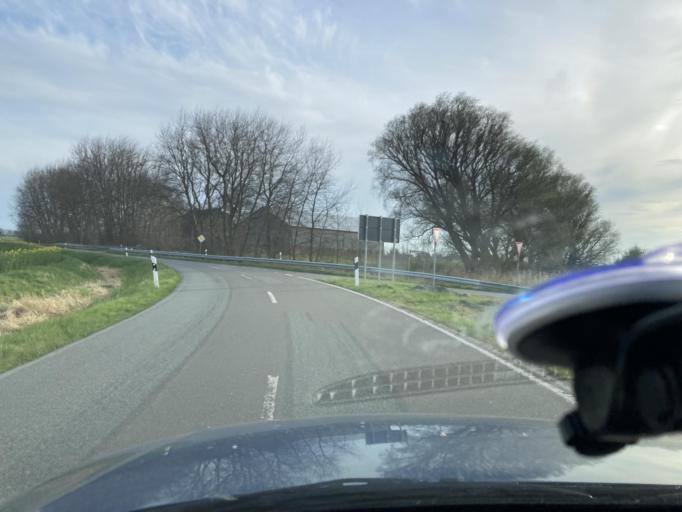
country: DE
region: Schleswig-Holstein
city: Schulp
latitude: 54.2532
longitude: 8.9448
